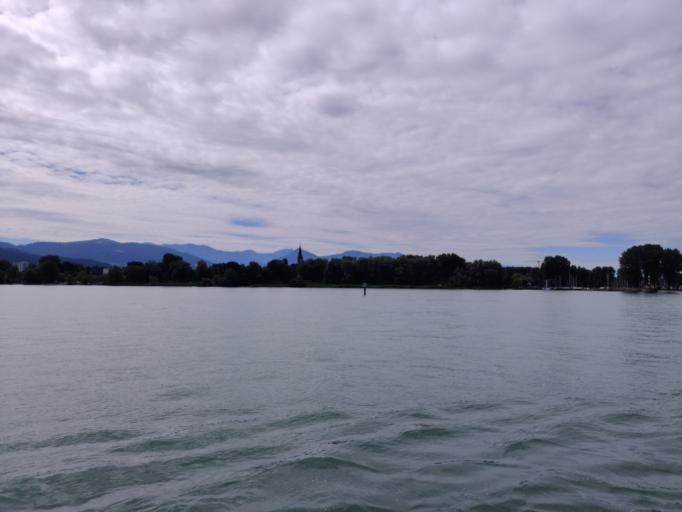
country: AT
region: Vorarlberg
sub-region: Politischer Bezirk Bregenz
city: Bregenz
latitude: 47.5108
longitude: 9.7202
